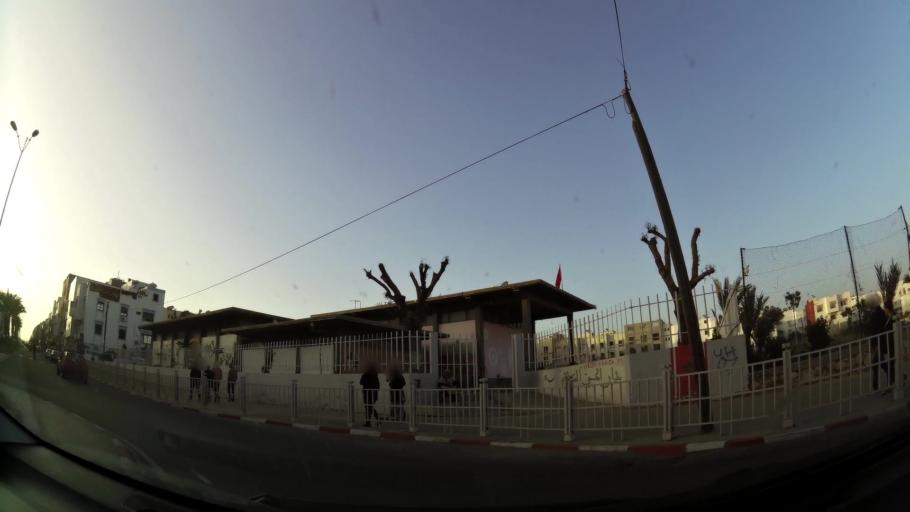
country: MA
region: Oued ed Dahab-Lagouira
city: Dakhla
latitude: 30.3993
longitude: -9.5505
